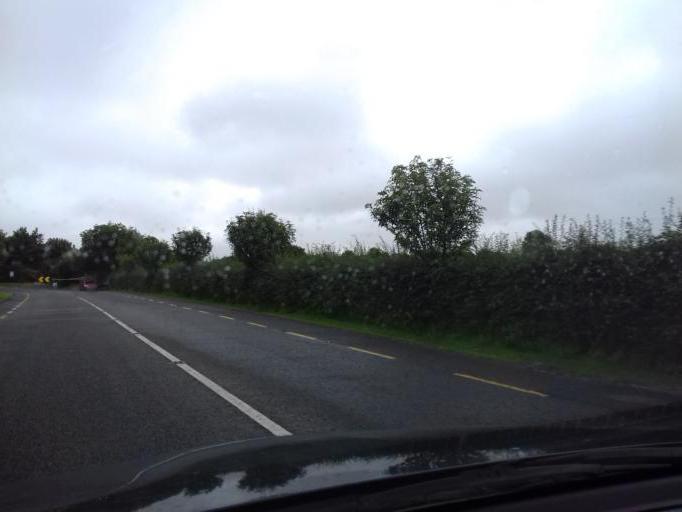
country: IE
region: Leinster
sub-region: County Carlow
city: Bagenalstown
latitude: 52.7434
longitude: -6.9702
